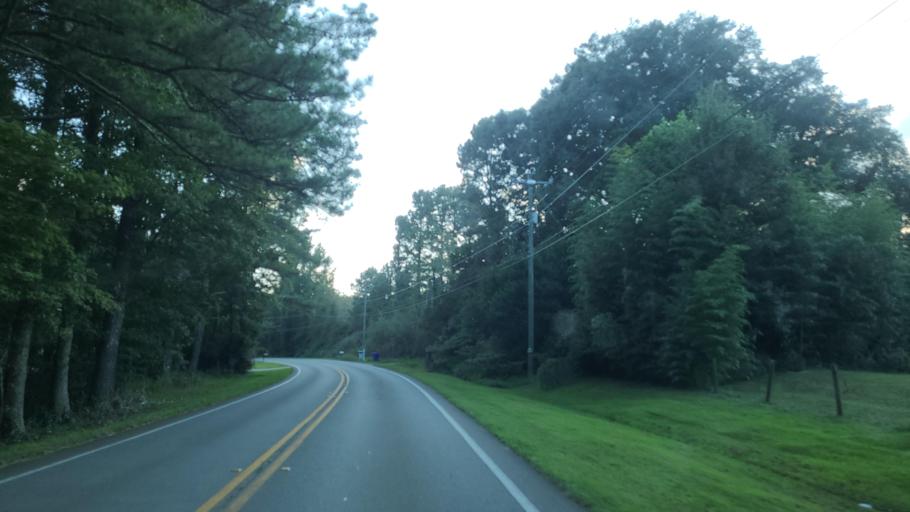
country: US
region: Georgia
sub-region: Fulton County
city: Milton
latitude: 34.1606
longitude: -84.3821
